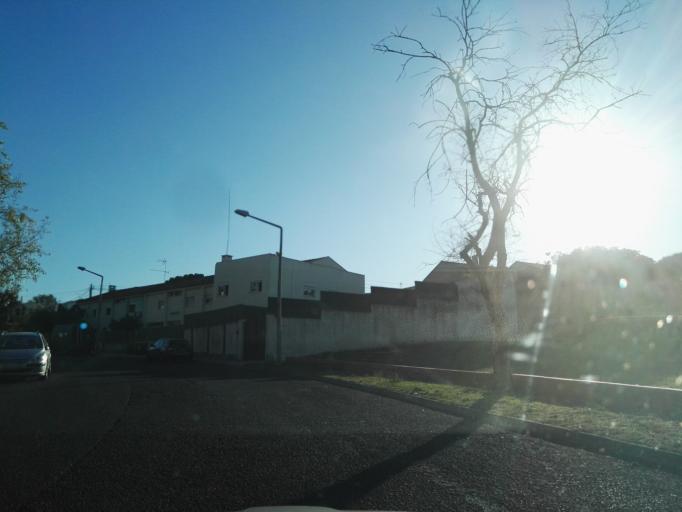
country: PT
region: Lisbon
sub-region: Loures
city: Moscavide
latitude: 38.7656
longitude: -9.1250
